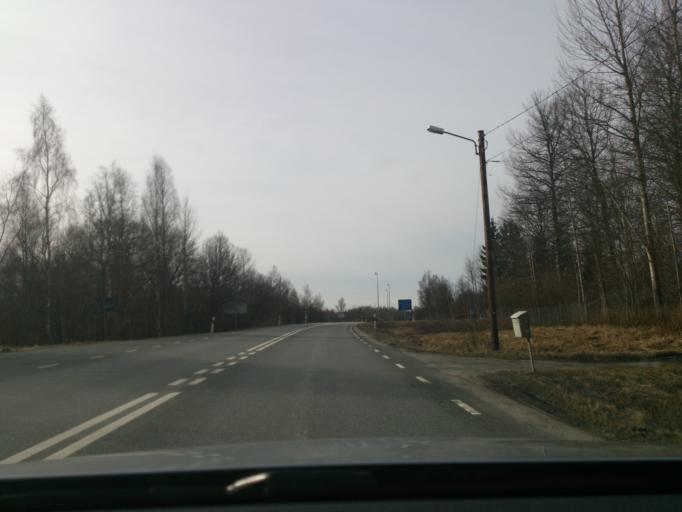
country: SE
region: Kronoberg
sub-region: Alvesta Kommun
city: Alvesta
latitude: 56.9246
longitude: 14.5595
